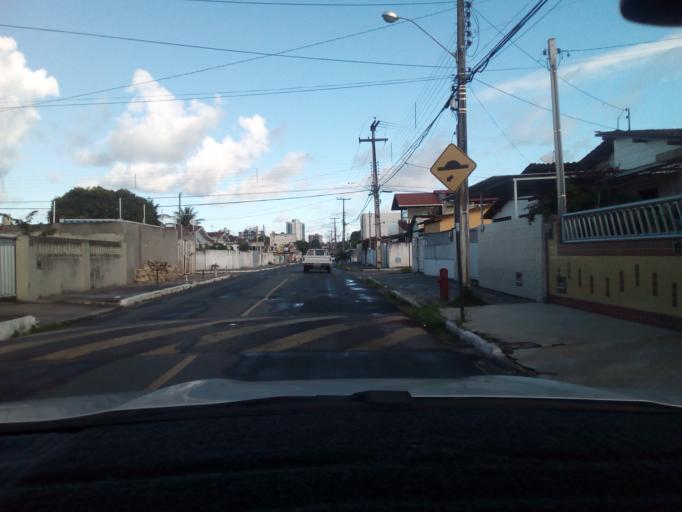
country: BR
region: Paraiba
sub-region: Joao Pessoa
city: Joao Pessoa
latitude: -7.1106
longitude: -34.8658
